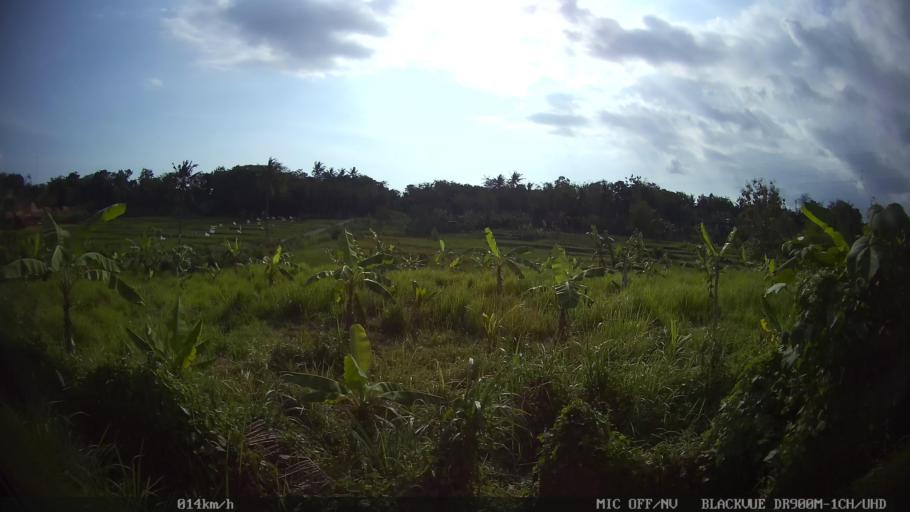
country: ID
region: Daerah Istimewa Yogyakarta
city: Kasihan
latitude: -7.8416
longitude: 110.3166
